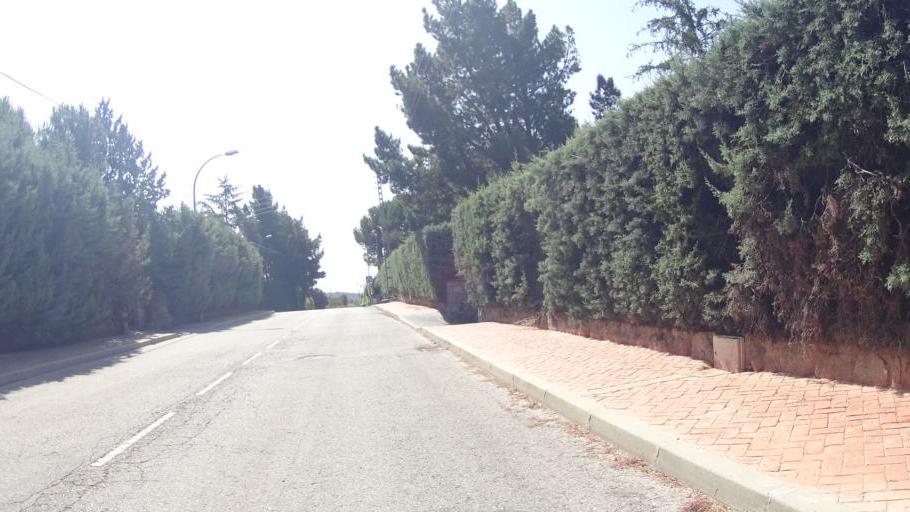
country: ES
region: Madrid
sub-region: Provincia de Madrid
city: Colmenarejo
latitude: 40.5672
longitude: -4.0117
